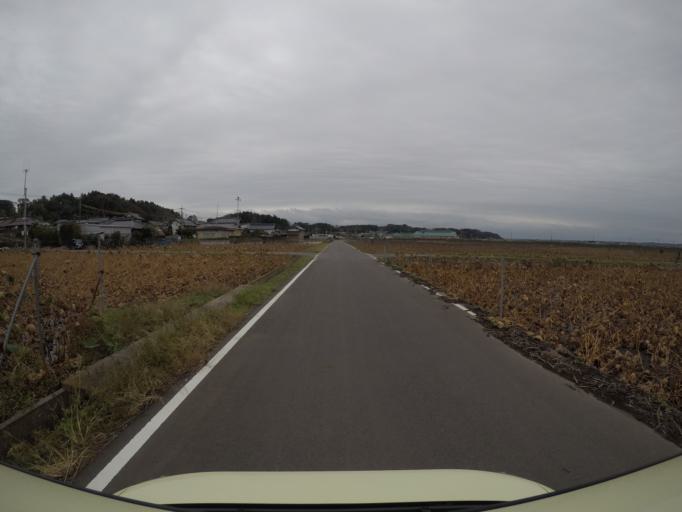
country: JP
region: Ibaraki
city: Ami
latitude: 36.0930
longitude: 140.2371
